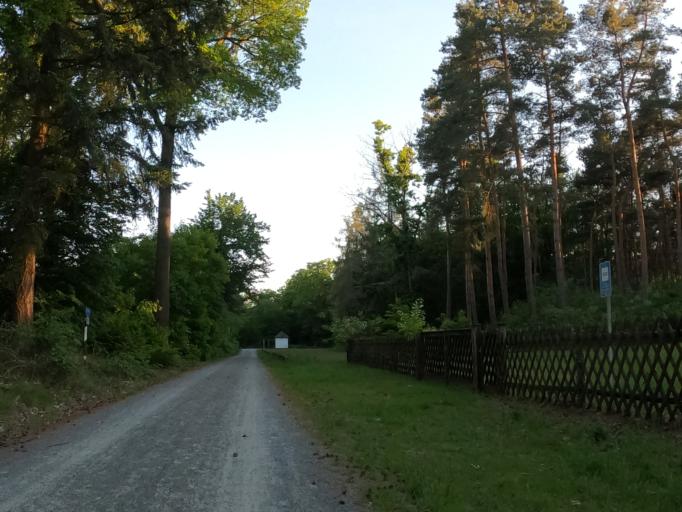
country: DE
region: Hesse
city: Kelsterbach
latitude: 50.0626
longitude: 8.5574
